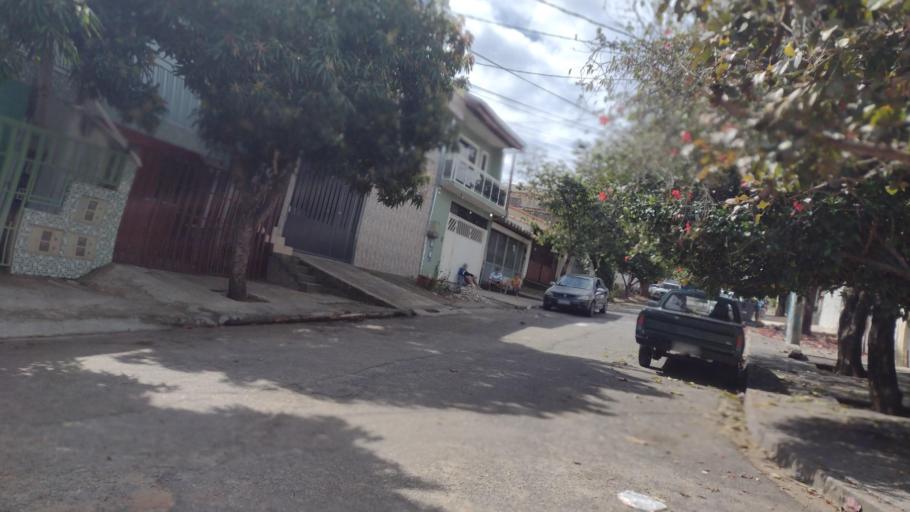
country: BR
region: Sao Paulo
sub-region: Sorocaba
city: Sorocaba
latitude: -23.4291
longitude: -47.4678
